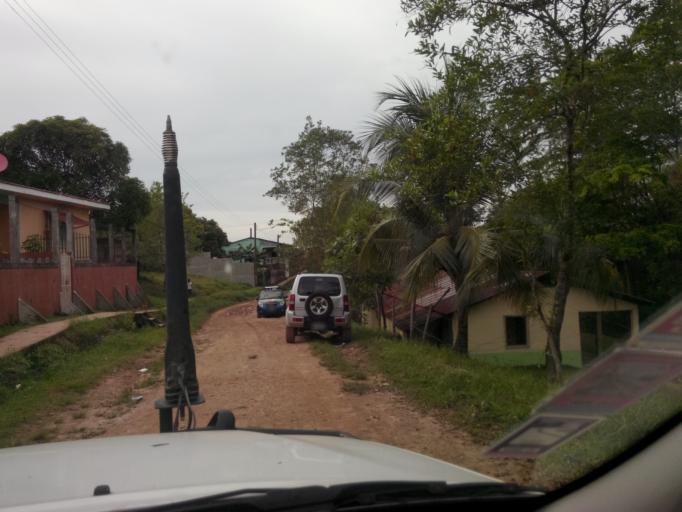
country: NI
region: Atlantico Sur
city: Bluefields
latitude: 12.0278
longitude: -83.7729
